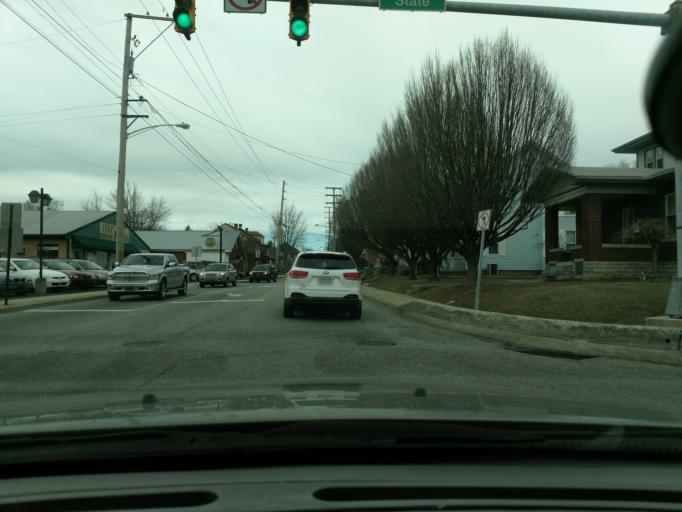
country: US
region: Pennsylvania
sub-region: Lebanon County
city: Lebanon
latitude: 40.3344
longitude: -76.4119
